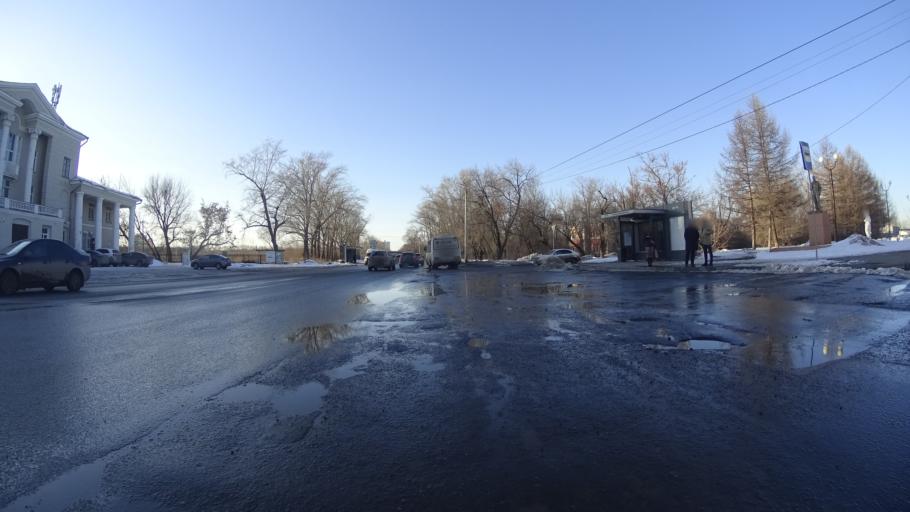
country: RU
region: Chelyabinsk
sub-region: Gorod Chelyabinsk
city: Chelyabinsk
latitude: 55.1304
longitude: 61.4646
